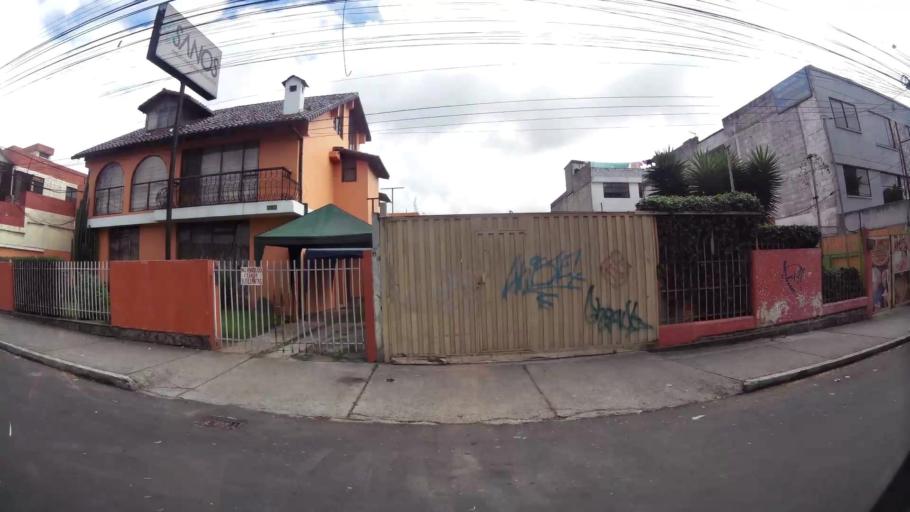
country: EC
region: Pichincha
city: Quito
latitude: -0.1561
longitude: -78.4897
